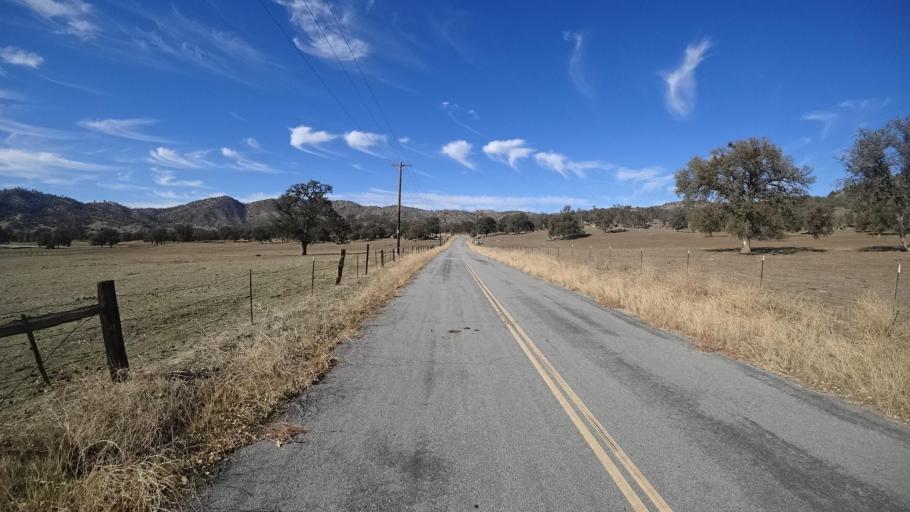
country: US
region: California
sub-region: Kern County
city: Alta Sierra
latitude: 35.6201
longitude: -118.7349
